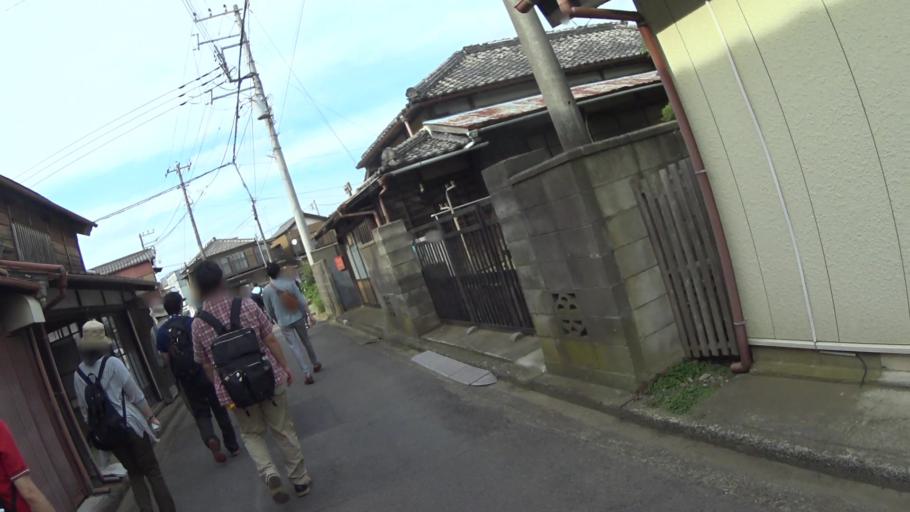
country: JP
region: Chiba
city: Sawara
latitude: 35.8875
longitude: 140.4992
